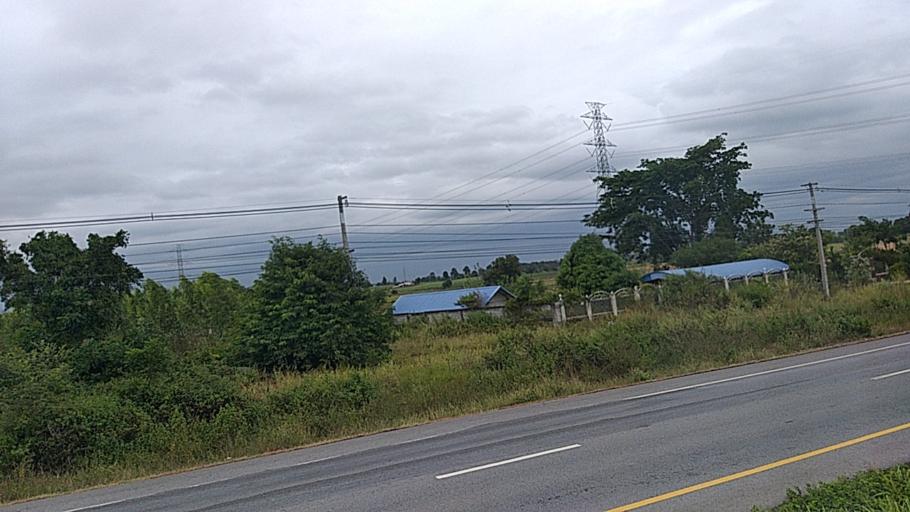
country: TH
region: Khon Kaen
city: Non Sila
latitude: 15.9390
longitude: 102.6759
